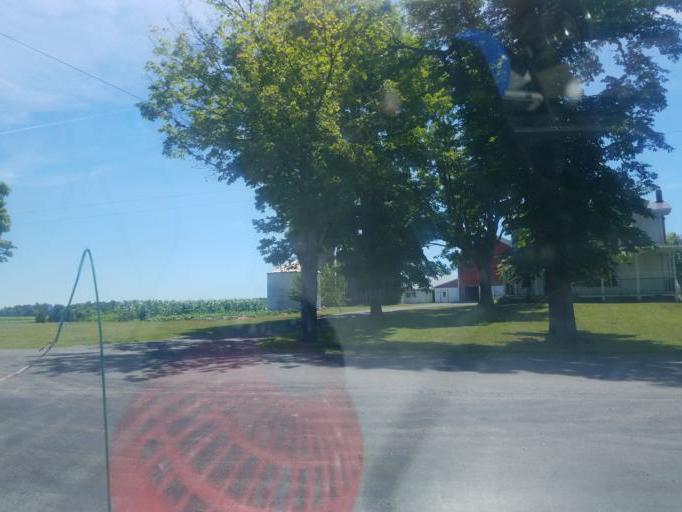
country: US
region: New York
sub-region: Yates County
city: Penn Yan
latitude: 42.6326
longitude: -77.0156
